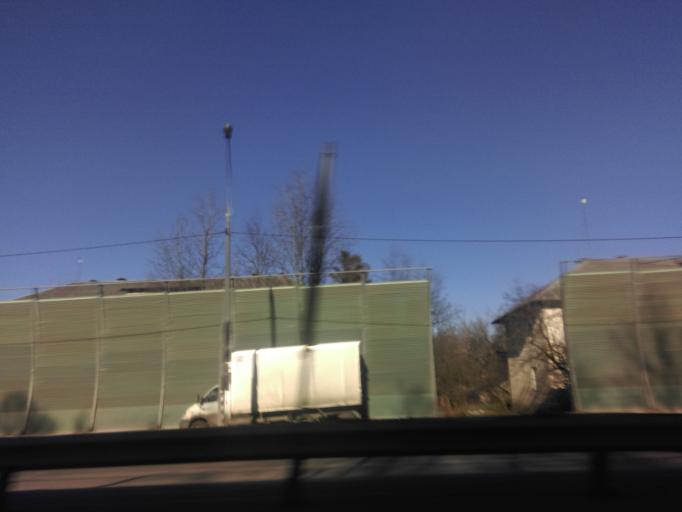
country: RU
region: Moscow
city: Novo-Peredelkino
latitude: 55.6794
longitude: 37.3220
